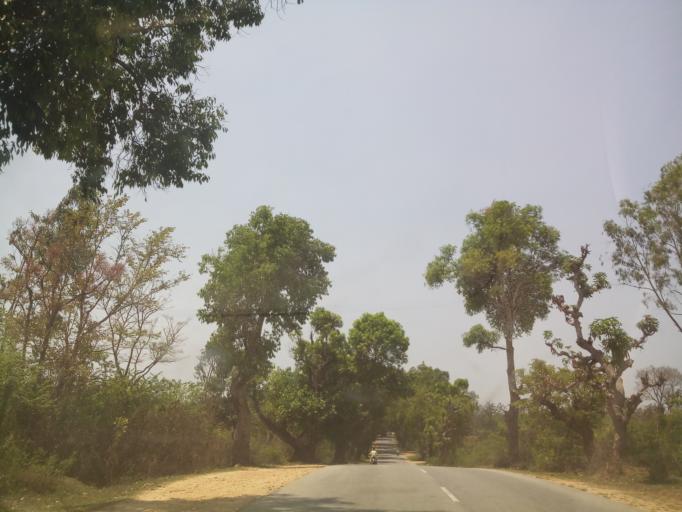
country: IN
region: Karnataka
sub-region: Hassan
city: Alur
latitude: 12.9554
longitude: 75.9128
